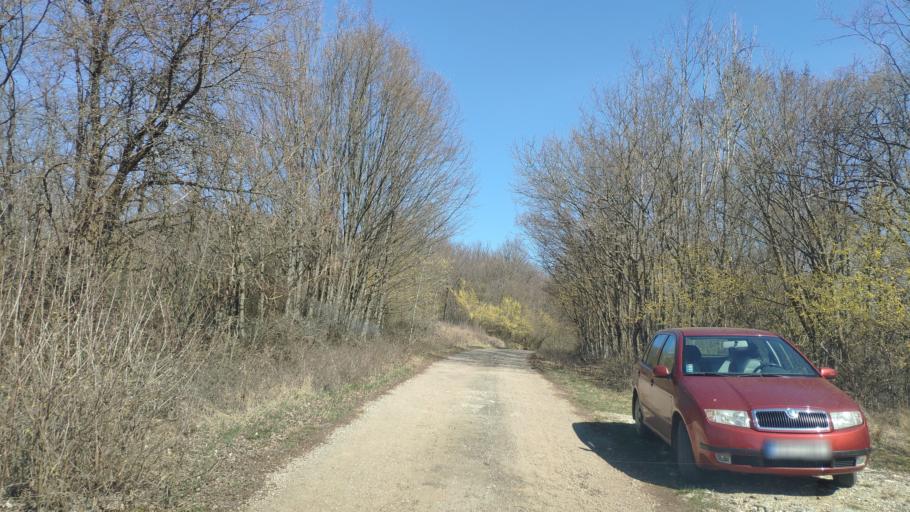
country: SK
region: Kosicky
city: Roznava
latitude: 48.5832
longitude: 20.4043
